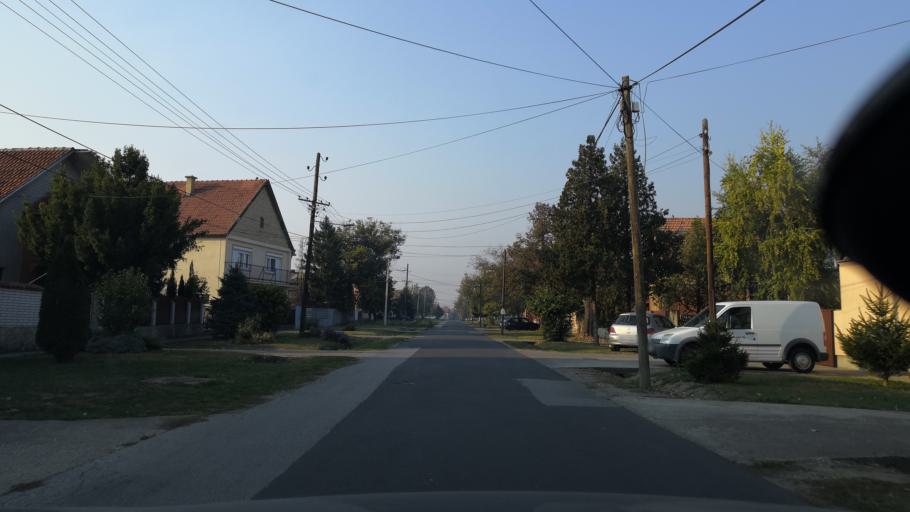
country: RS
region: Autonomna Pokrajina Vojvodina
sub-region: Sremski Okrug
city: Stara Pazova
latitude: 44.9917
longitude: 20.1481
